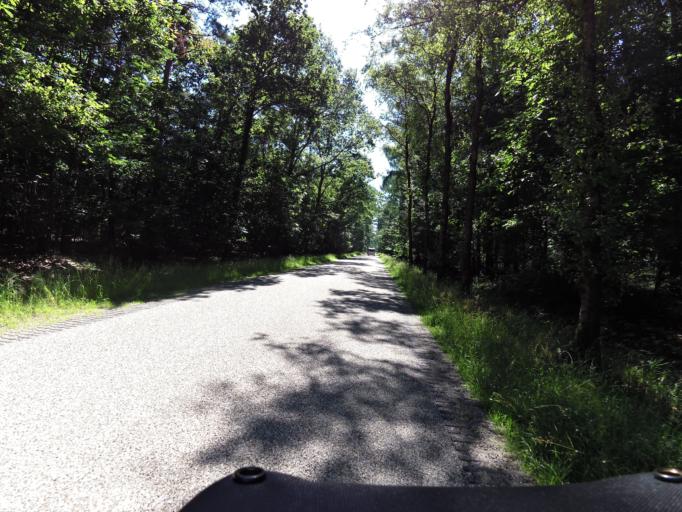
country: NL
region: Overijssel
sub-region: Gemeente Twenterand
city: Den Ham
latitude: 52.5374
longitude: 6.4914
